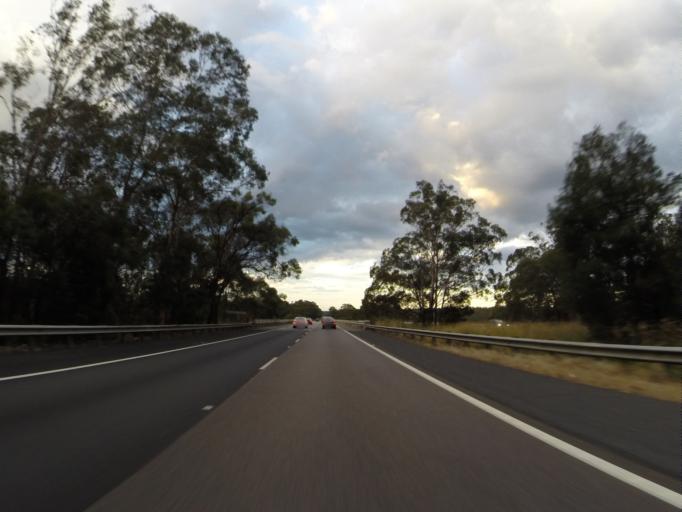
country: AU
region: New South Wales
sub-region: Wollondilly
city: Douglas Park
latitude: -34.2115
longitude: 150.6889
